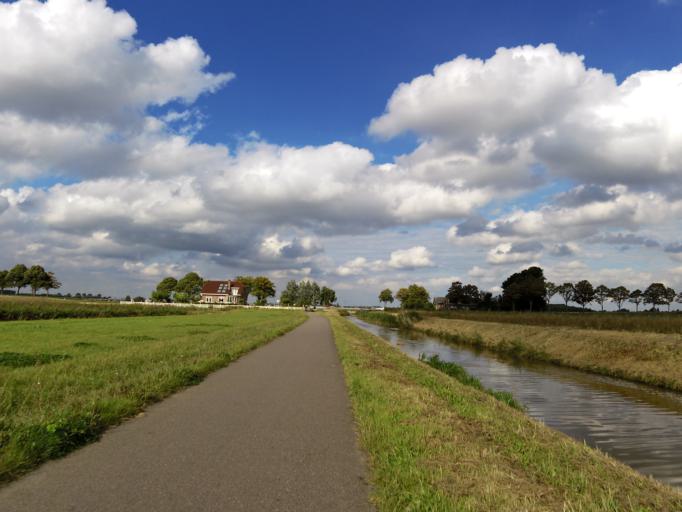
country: NL
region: South Holland
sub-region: Gemeente Waddinxveen
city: Groenswaard
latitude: 52.0752
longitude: 4.6069
